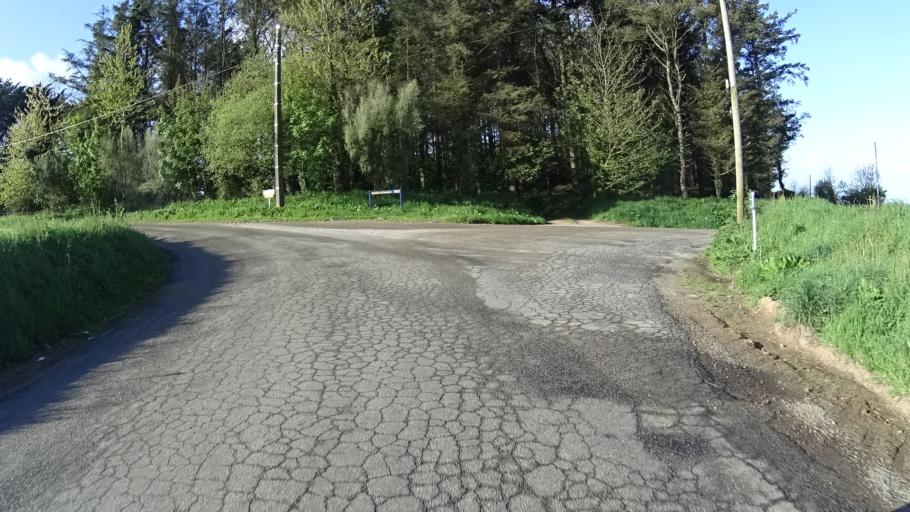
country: FR
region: Brittany
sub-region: Departement du Finistere
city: Ploumoguer
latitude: 48.4251
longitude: -4.7050
